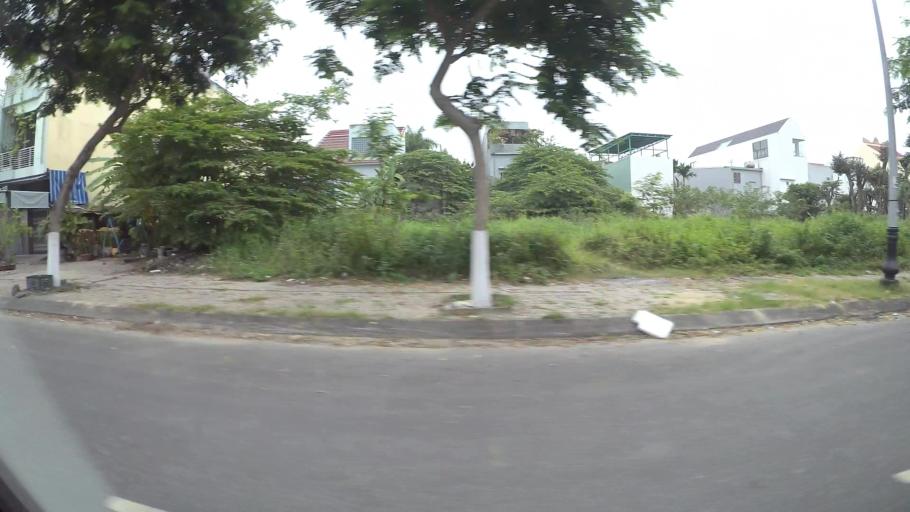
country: VN
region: Da Nang
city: Ngu Hanh Son
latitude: 16.0319
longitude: 108.2294
